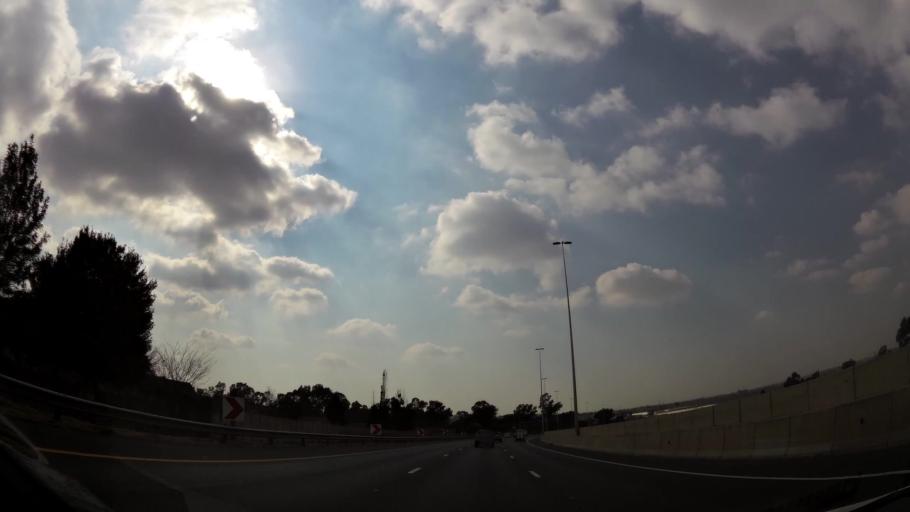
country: ZA
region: Gauteng
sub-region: Ekurhuleni Metropolitan Municipality
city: Benoni
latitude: -26.1640
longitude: 28.3586
